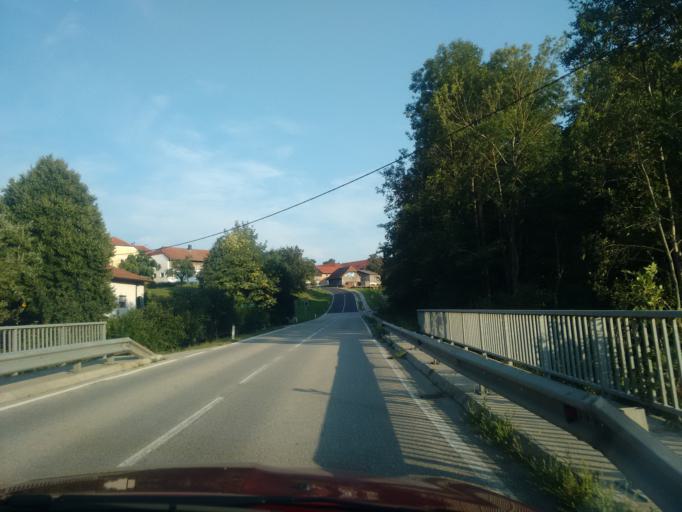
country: AT
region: Upper Austria
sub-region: Politischer Bezirk Vocklabruck
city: Wolfsegg am Hausruck
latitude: 48.1619
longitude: 13.6642
